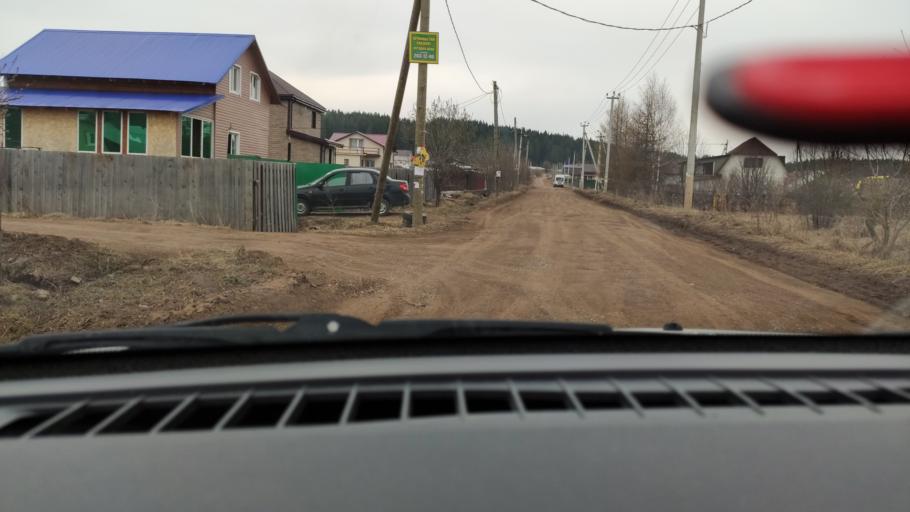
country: RU
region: Perm
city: Kultayevo
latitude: 57.8970
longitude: 56.0142
